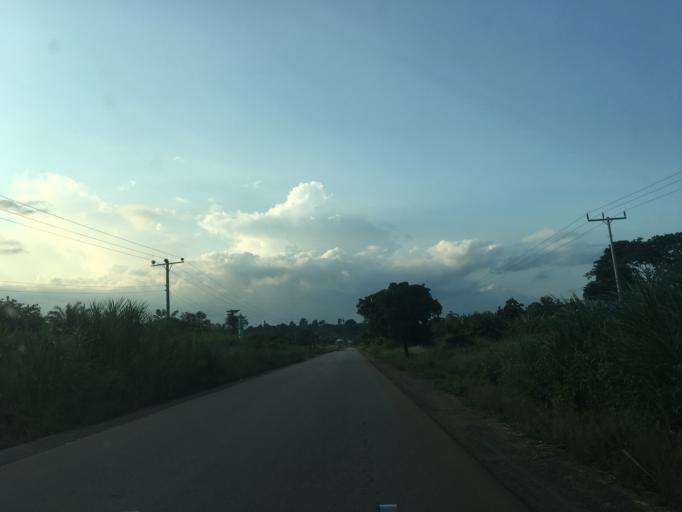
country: GH
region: Western
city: Bibiani
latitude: 6.6158
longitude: -2.4086
